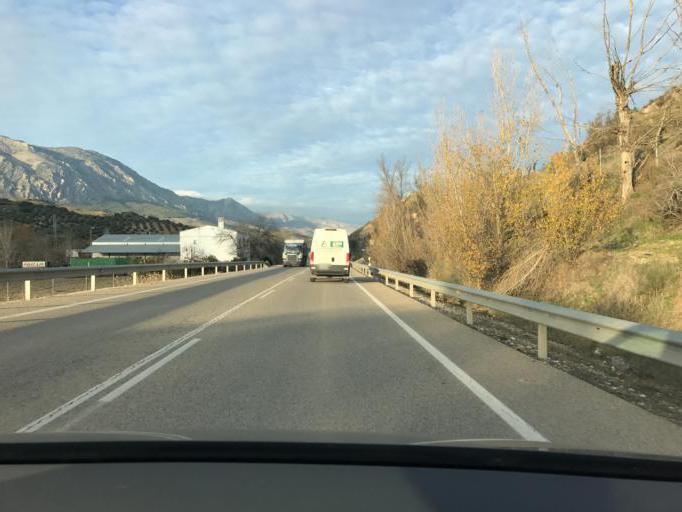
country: ES
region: Andalusia
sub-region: Provincia de Jaen
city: Huelma
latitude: 37.6529
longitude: -3.4210
